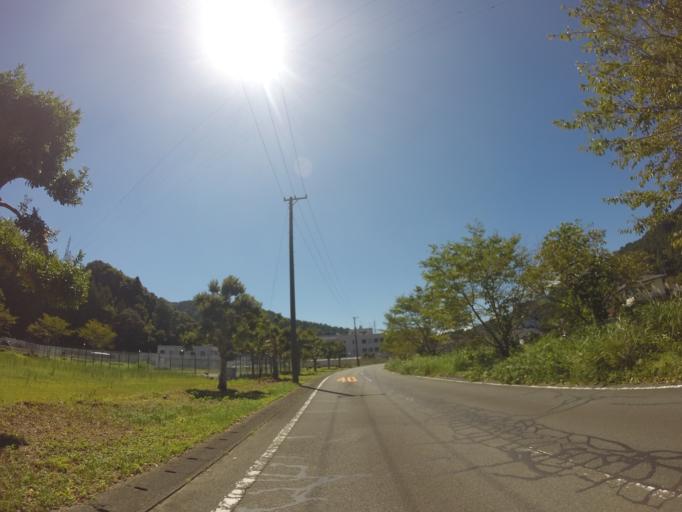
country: JP
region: Shizuoka
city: Kanaya
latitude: 34.8793
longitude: 138.1416
